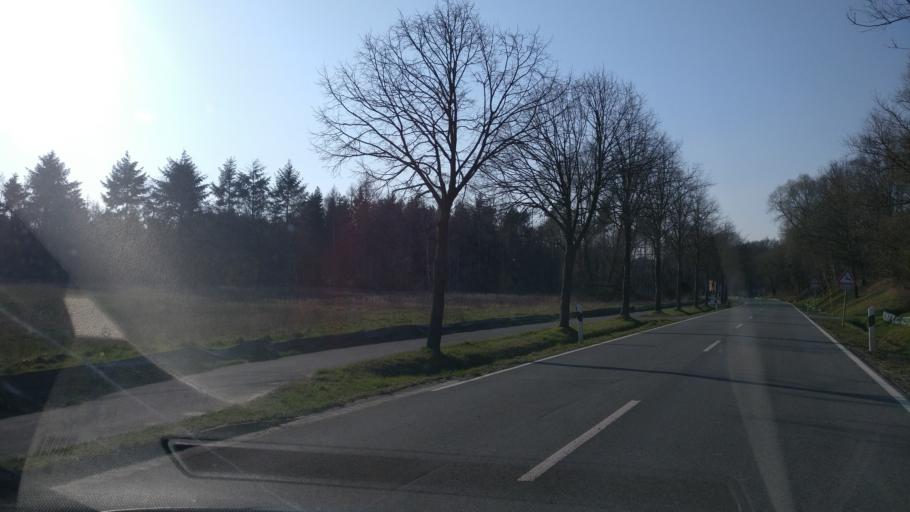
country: DE
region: North Rhine-Westphalia
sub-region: Regierungsbezirk Detmold
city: Lage
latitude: 52.0009
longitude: 8.7692
